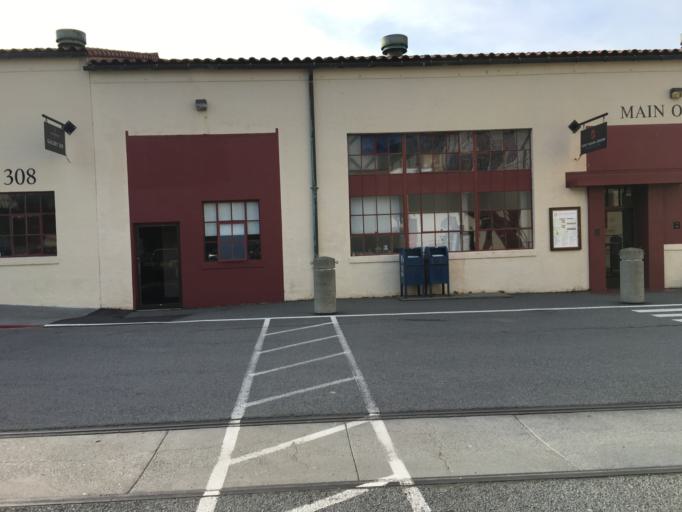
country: US
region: California
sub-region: San Francisco County
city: San Francisco
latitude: 37.8064
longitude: -122.4318
